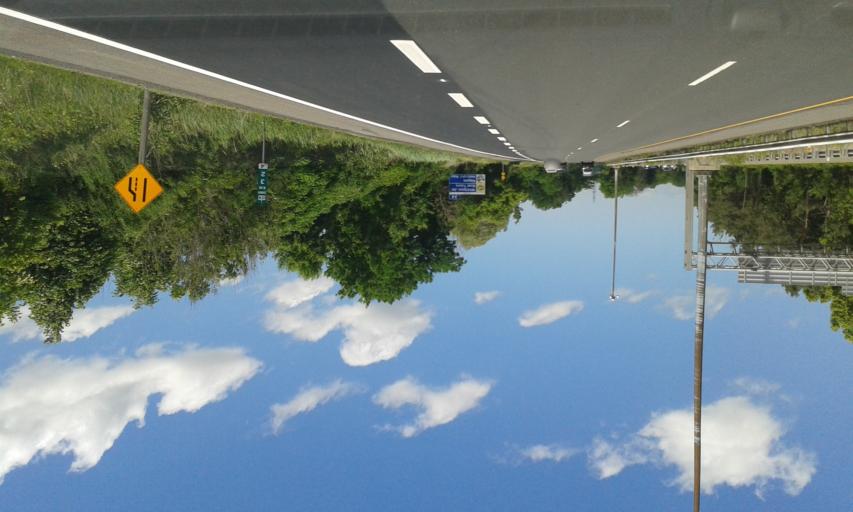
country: CA
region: Ontario
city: Niagara Falls
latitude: 43.1185
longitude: -79.1204
